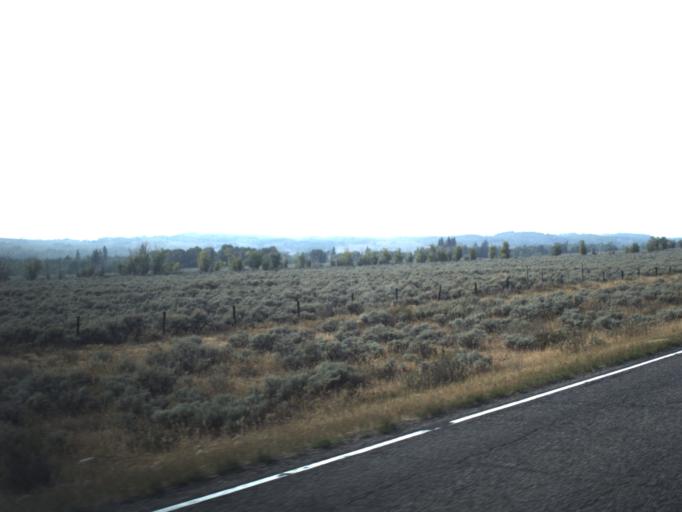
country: US
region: Wyoming
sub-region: Uinta County
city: Evanston
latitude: 40.9759
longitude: -110.8524
